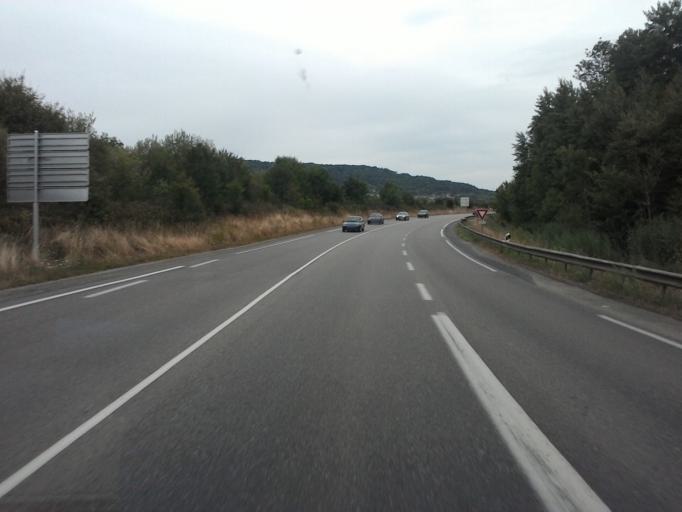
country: FR
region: Lorraine
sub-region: Departement de Meurthe-et-Moselle
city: Pont-Saint-Vincent
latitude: 48.6009
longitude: 6.1169
